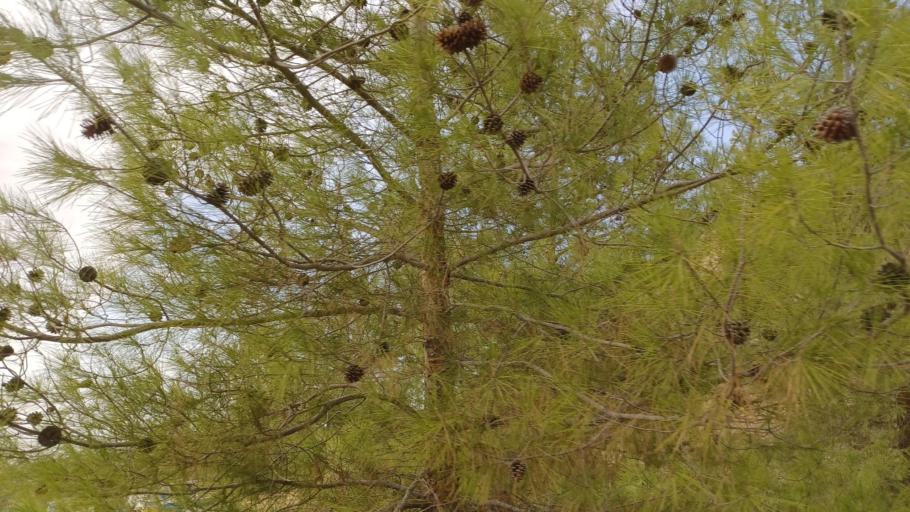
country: CY
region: Lefkosia
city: Klirou
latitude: 35.0420
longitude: 33.1051
